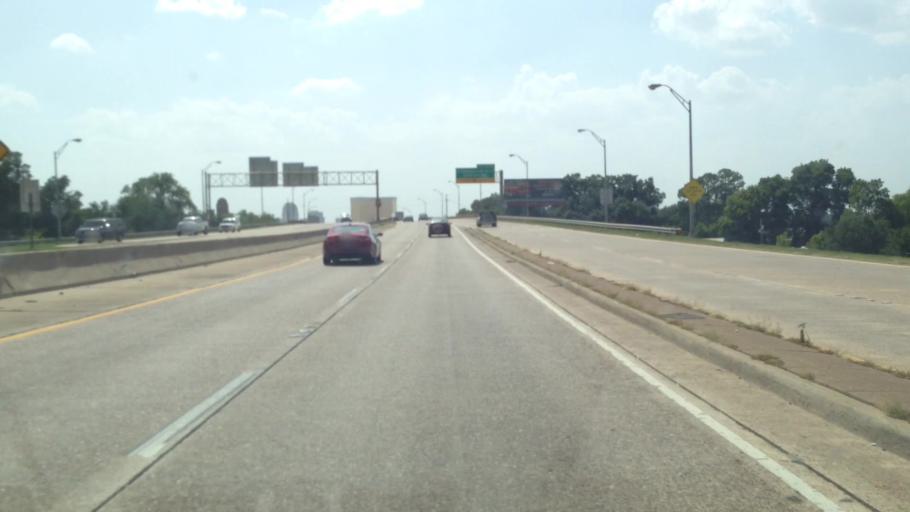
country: US
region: Louisiana
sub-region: Bossier Parish
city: Bossier City
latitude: 32.5136
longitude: -93.7186
